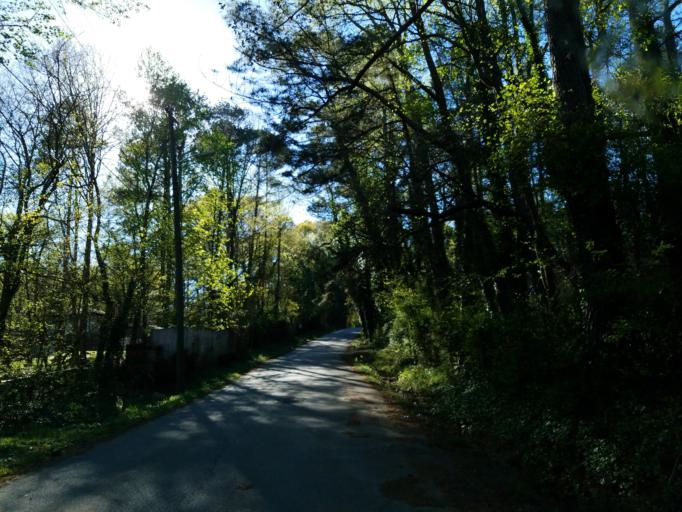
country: US
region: Georgia
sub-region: Cobb County
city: Marietta
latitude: 33.9618
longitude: -84.5039
